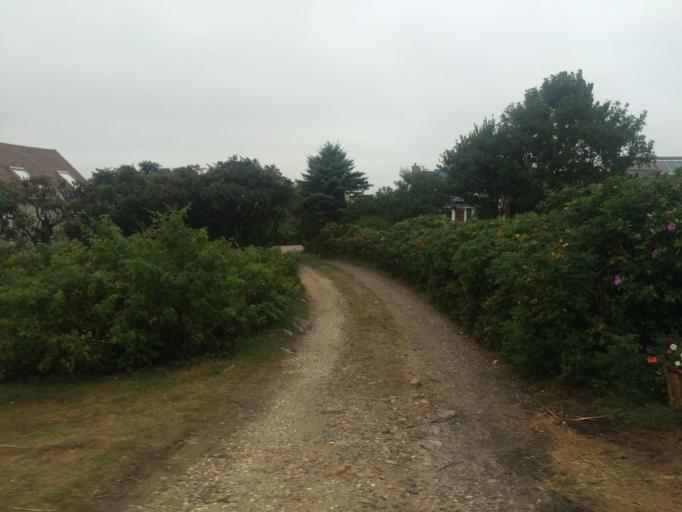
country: US
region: Massachusetts
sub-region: Plymouth County
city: Plymouth
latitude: 42.0038
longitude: -70.6019
